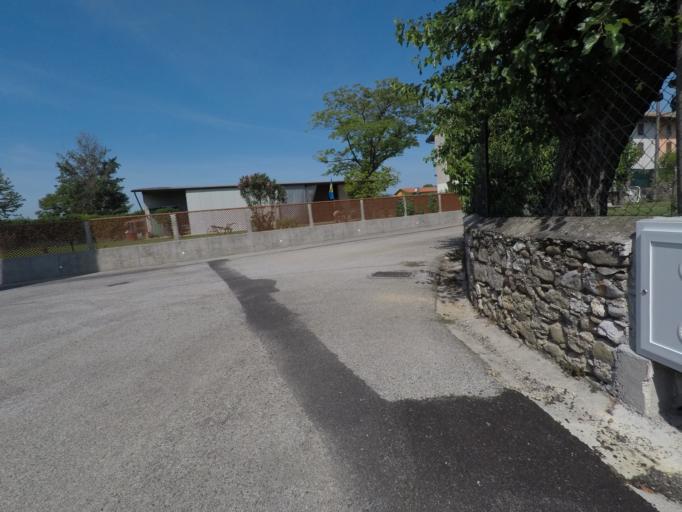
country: IT
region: Friuli Venezia Giulia
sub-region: Provincia di Udine
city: Coseano
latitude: 46.0703
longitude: 13.0232
